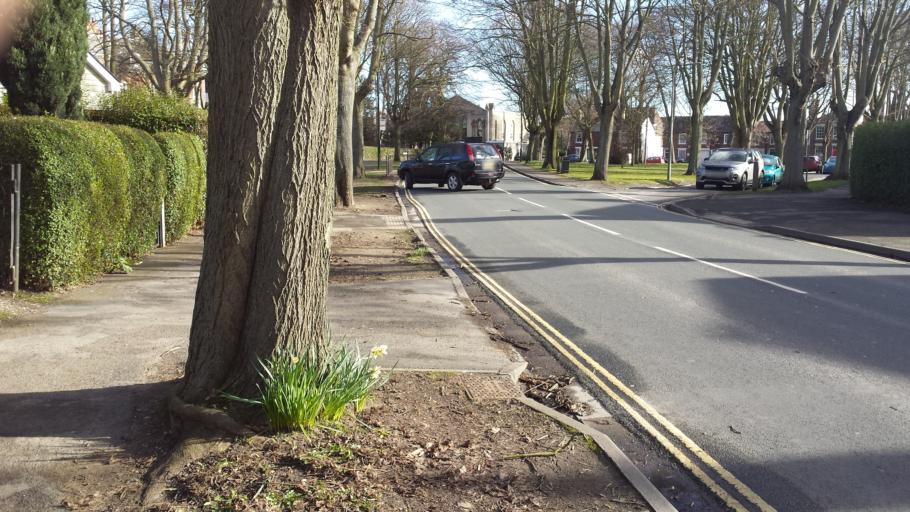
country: GB
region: England
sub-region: East Riding of Yorkshire
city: Beverley
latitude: 53.8385
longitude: -0.4326
